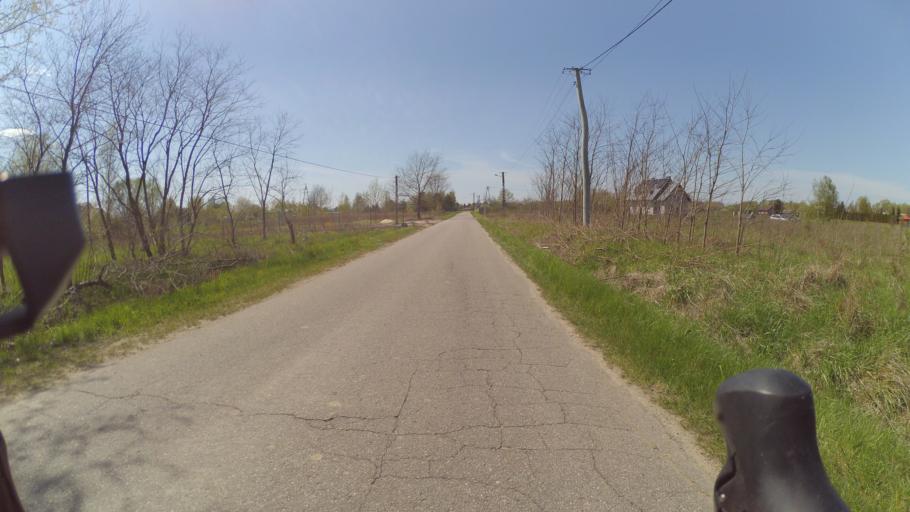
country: PL
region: Masovian Voivodeship
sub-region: Powiat nowodworski
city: Zakroczym
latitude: 52.4158
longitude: 20.5384
